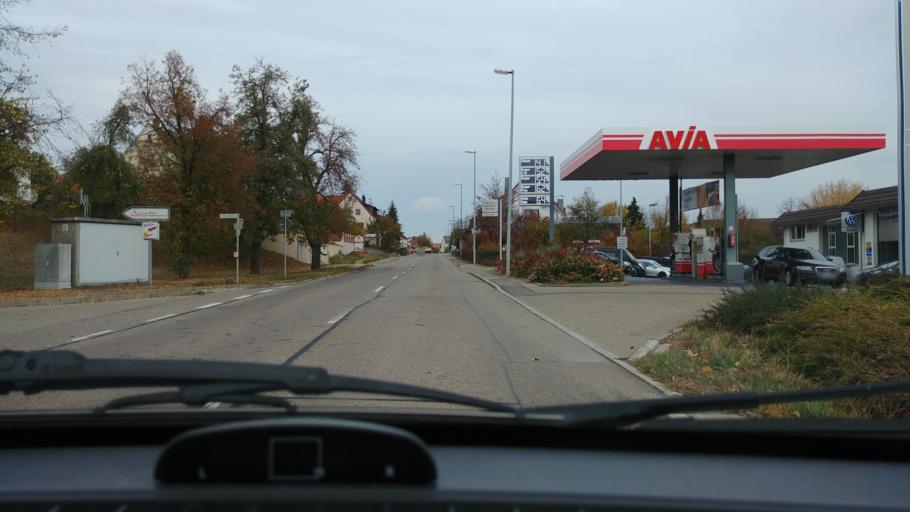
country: DE
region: Baden-Wuerttemberg
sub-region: Regierungsbezirk Stuttgart
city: Stimpfach
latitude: 49.0536
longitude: 10.0819
